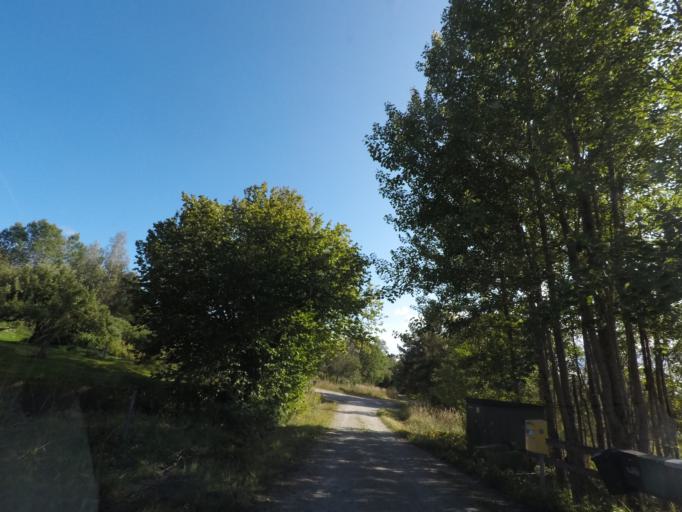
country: SE
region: Vaestmanland
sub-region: Skinnskattebergs Kommun
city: Skinnskatteberg
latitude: 59.8268
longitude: 15.5262
